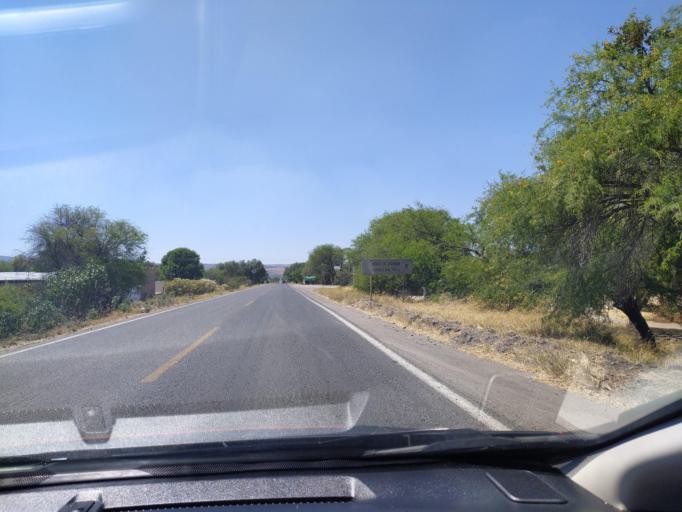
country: MX
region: Guanajuato
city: Ciudad Manuel Doblado
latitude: 20.7410
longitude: -101.9254
